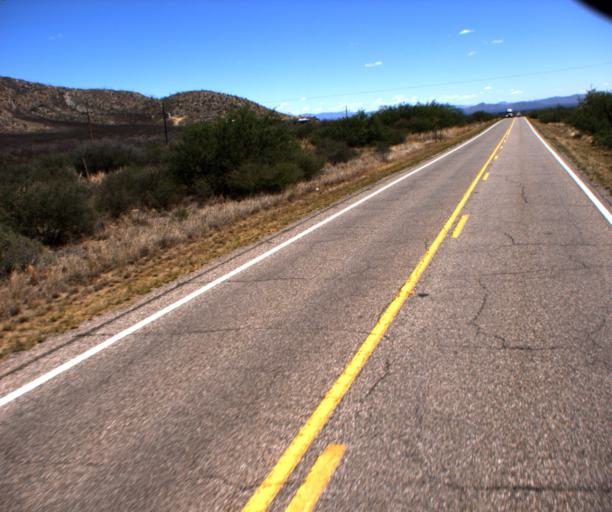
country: US
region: Arizona
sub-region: Cochise County
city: Huachuca City
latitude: 31.6918
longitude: -110.3916
